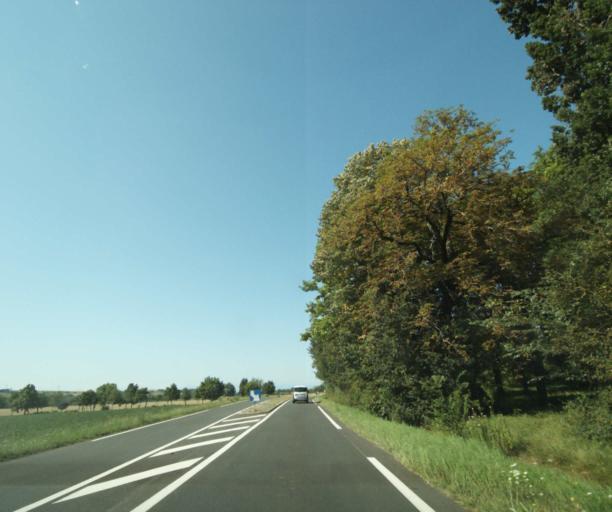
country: FR
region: Midi-Pyrenees
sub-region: Departement de la Haute-Garonne
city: Beaumont-sur-Leze
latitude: 43.3953
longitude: 1.3586
